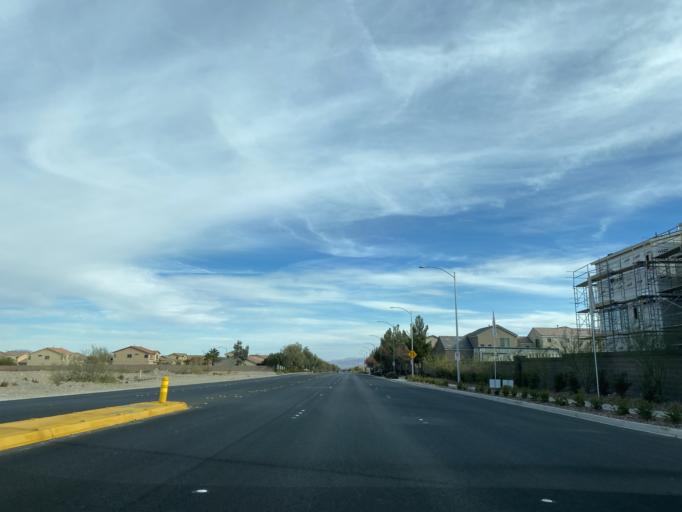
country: US
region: Nevada
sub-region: Clark County
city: Enterprise
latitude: 36.0410
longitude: -115.2599
